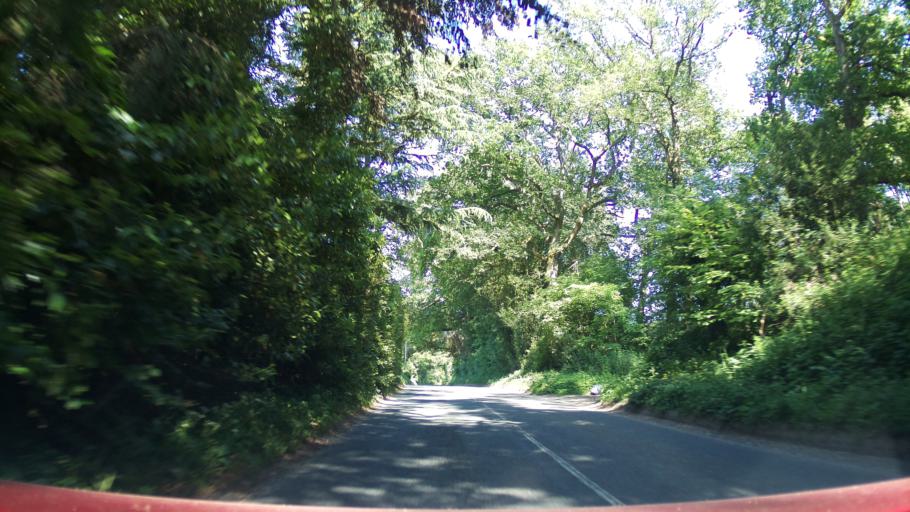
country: GB
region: England
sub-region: Hampshire
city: Andover
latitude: 51.2165
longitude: -1.4001
